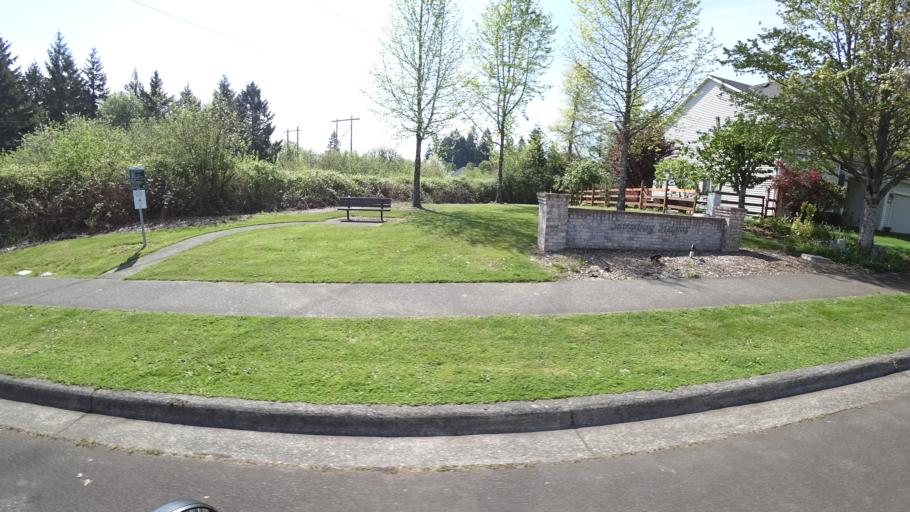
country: US
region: Oregon
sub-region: Washington County
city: Aloha
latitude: 45.4578
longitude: -122.8417
